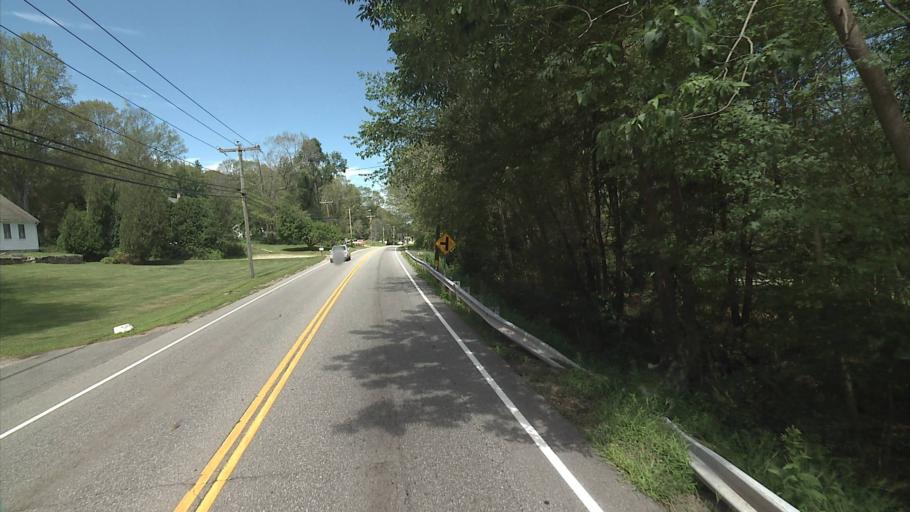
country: US
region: Connecticut
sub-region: Tolland County
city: Mansfield City
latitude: 41.7575
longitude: -72.1949
